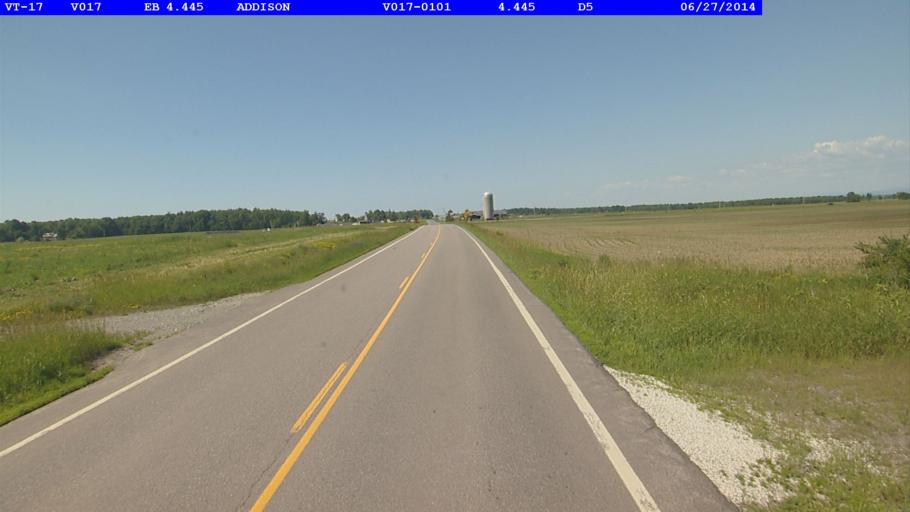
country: US
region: New York
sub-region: Essex County
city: Port Henry
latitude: 44.0776
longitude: -73.3764
